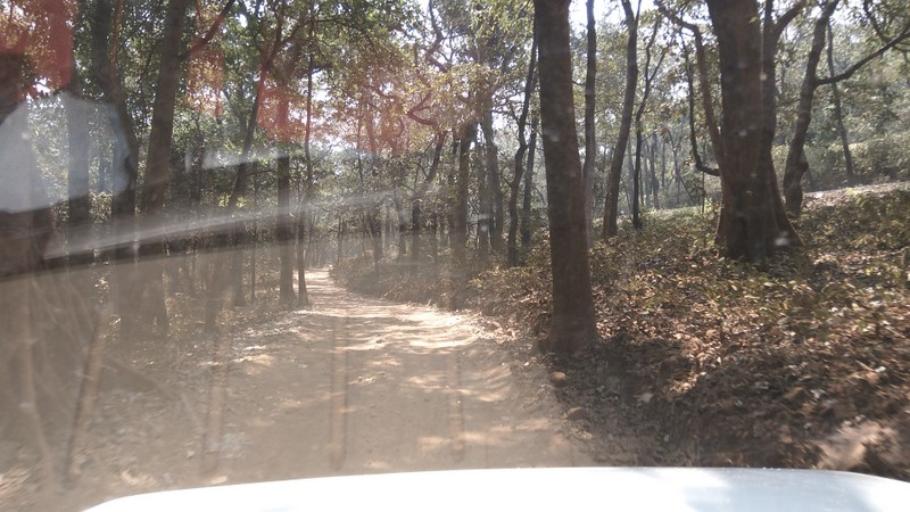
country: IN
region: Goa
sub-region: South Goa
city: Sanguem
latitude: 15.3286
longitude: 74.2813
